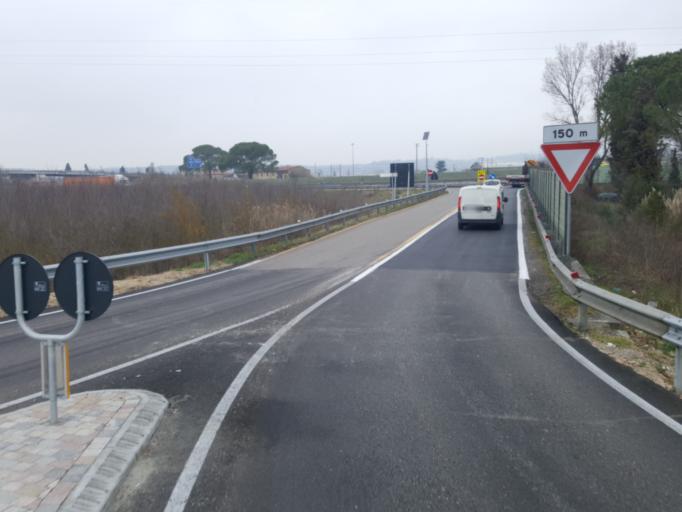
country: IT
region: Tuscany
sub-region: Province of Florence
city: Montelupo Fiorentino
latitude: 43.7176
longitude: 10.9856
